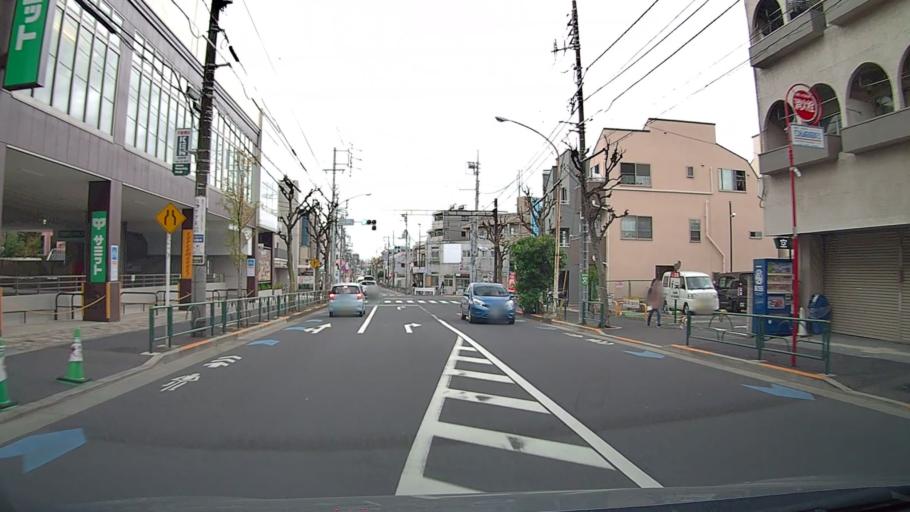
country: JP
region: Tokyo
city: Musashino
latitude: 35.7164
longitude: 139.6277
